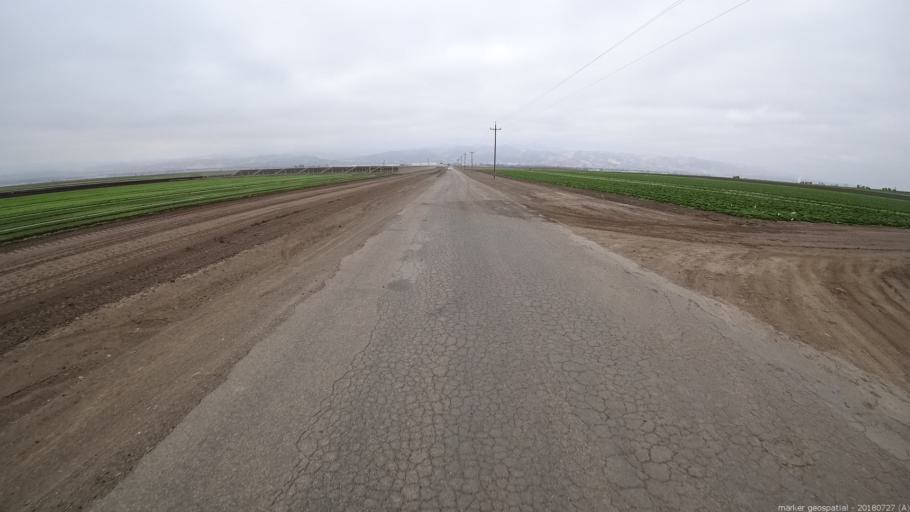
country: US
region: California
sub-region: Monterey County
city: King City
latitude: 36.2140
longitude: -121.0965
